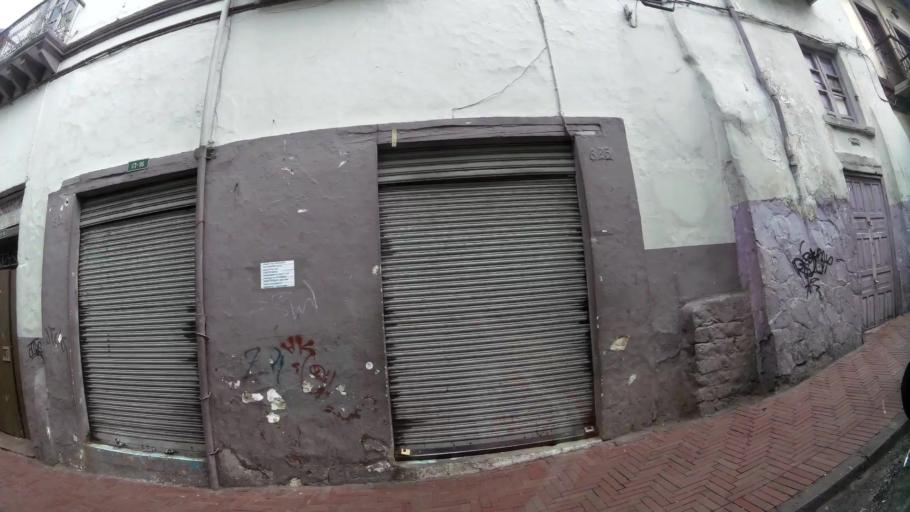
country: EC
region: Pichincha
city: Quito
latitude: -0.2213
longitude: -78.5180
